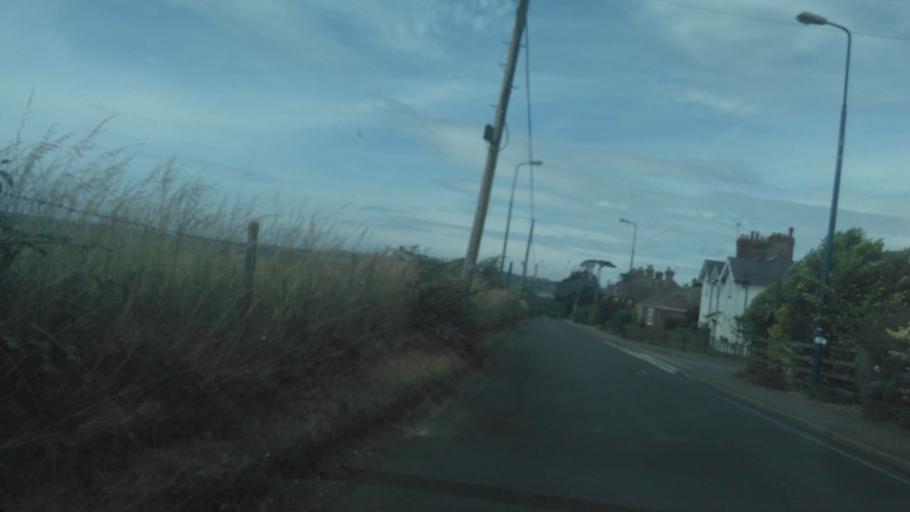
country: GB
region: England
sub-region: Kent
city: Chartham
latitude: 51.2473
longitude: 1.0231
